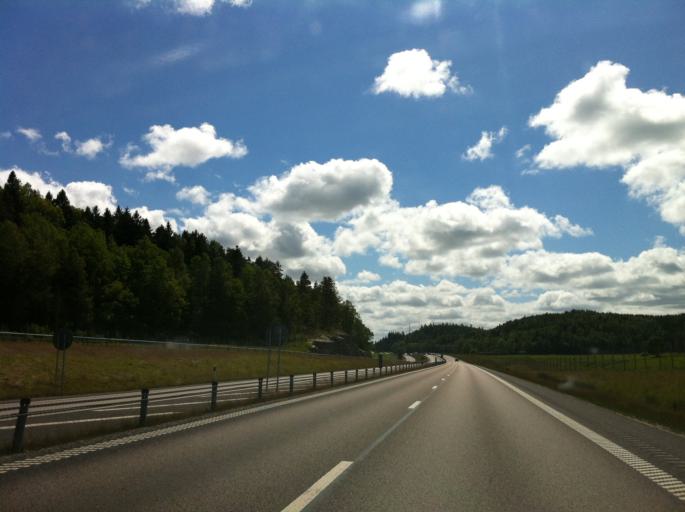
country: SE
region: Vaestra Goetaland
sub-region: Lilla Edets Kommun
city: Lilla Edet
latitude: 58.1966
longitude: 12.1499
